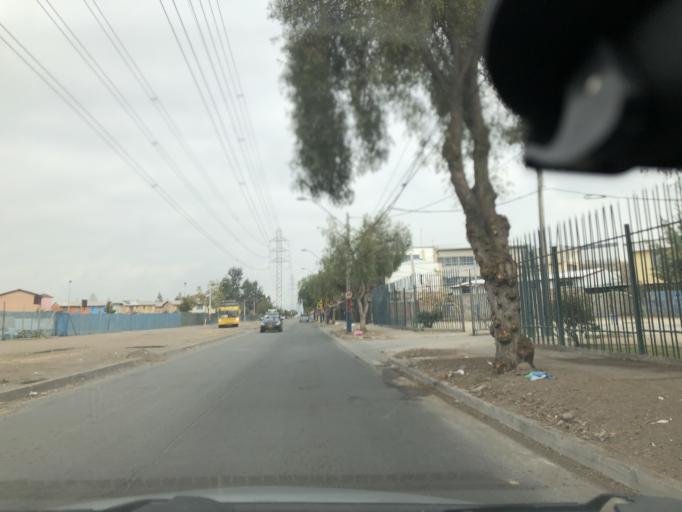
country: CL
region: Santiago Metropolitan
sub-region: Provincia de Cordillera
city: Puente Alto
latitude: -33.5934
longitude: -70.6005
